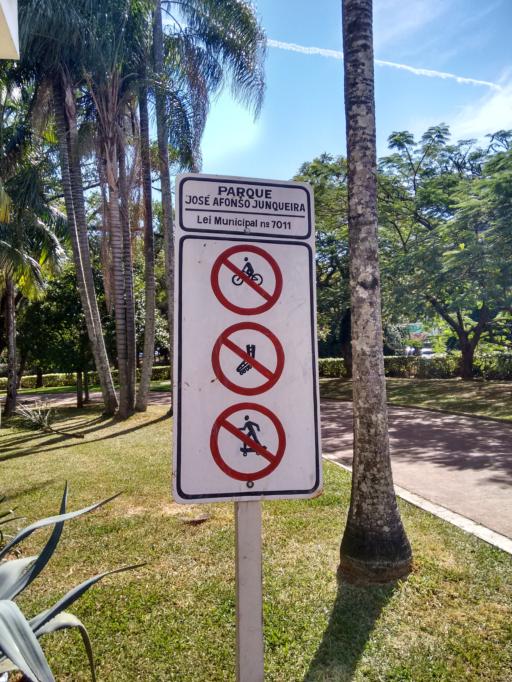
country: BR
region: Minas Gerais
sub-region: Pocos De Caldas
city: Pocos de Caldas
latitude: -21.7852
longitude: -46.5704
